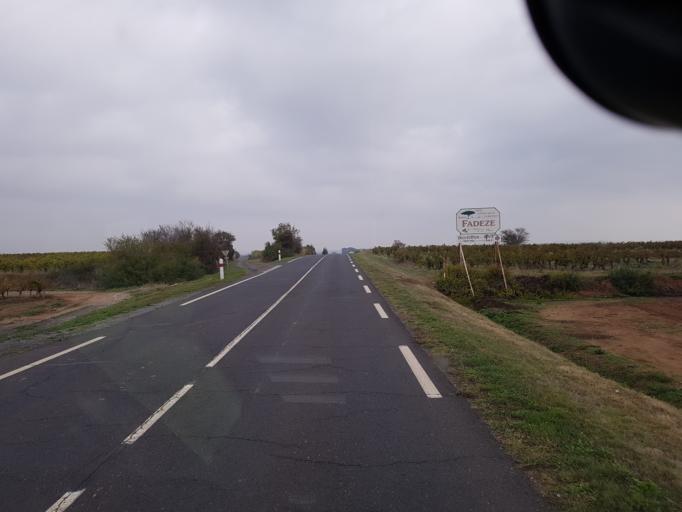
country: FR
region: Languedoc-Roussillon
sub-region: Departement de l'Herault
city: Marseillan
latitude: 43.3738
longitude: 3.5336
